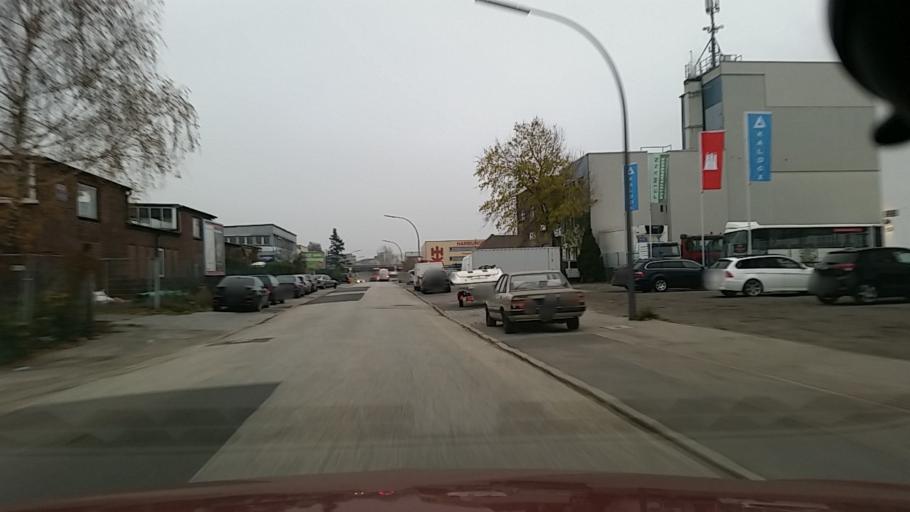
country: DE
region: Hamburg
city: Rothenburgsort
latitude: 53.5379
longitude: 10.0657
